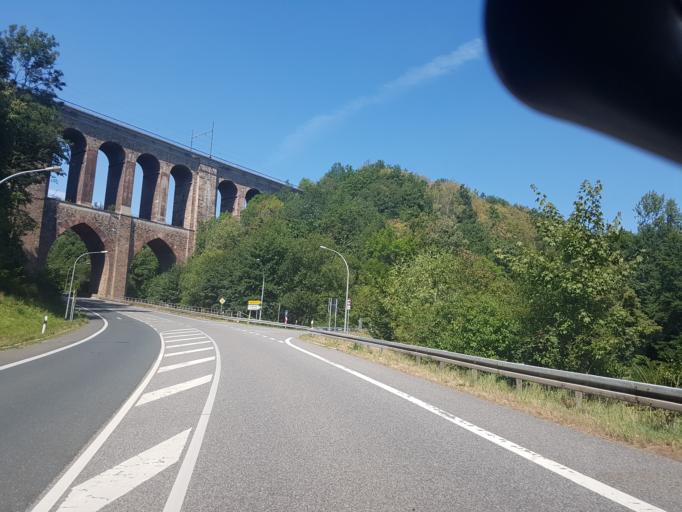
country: DE
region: Saxony
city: Waldheim
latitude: 51.0804
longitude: 13.0148
